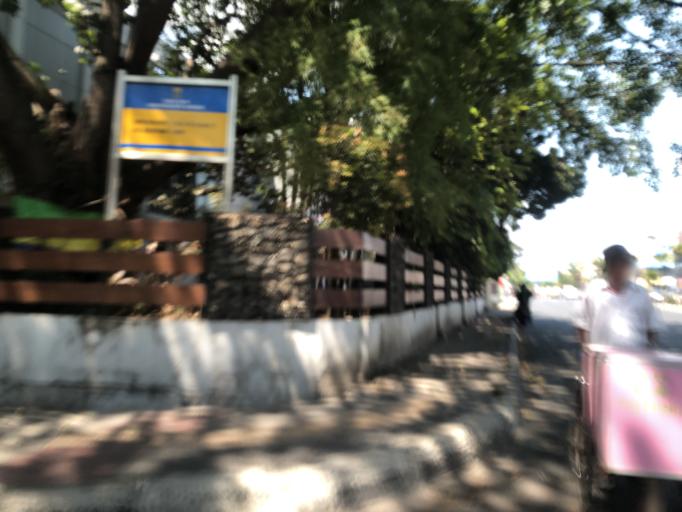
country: ID
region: West Java
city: Bandung
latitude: -6.9139
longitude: 107.6334
